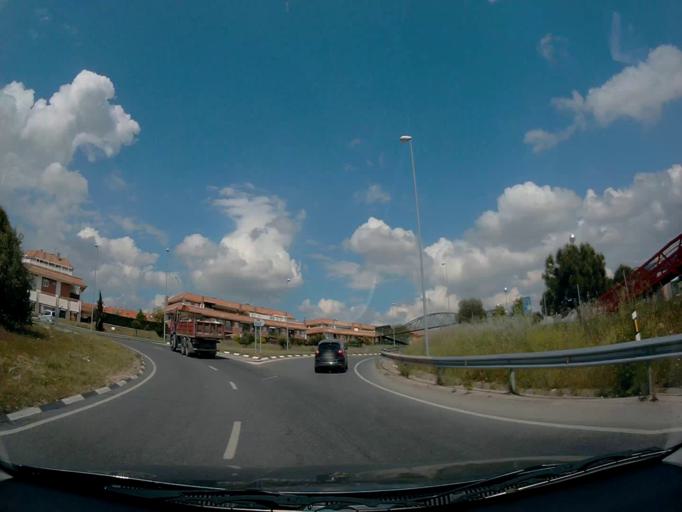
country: ES
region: Madrid
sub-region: Provincia de Madrid
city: Villaviciosa de Odon
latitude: 40.3510
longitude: -3.9032
